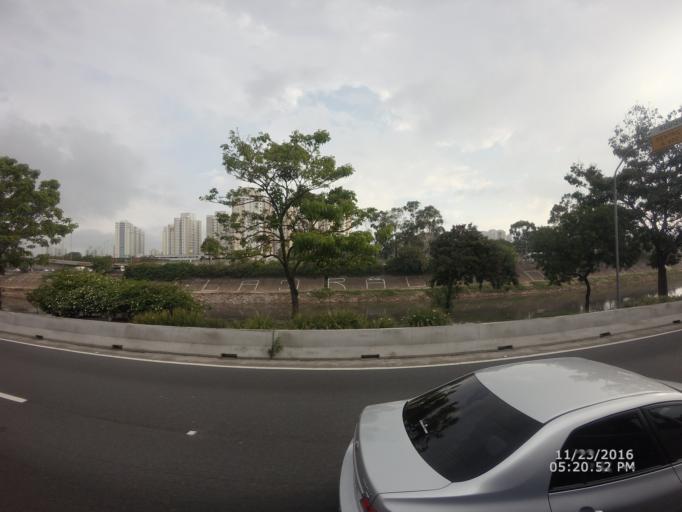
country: BR
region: Sao Paulo
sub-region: Guarulhos
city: Guarulhos
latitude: -23.5230
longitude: -46.5621
